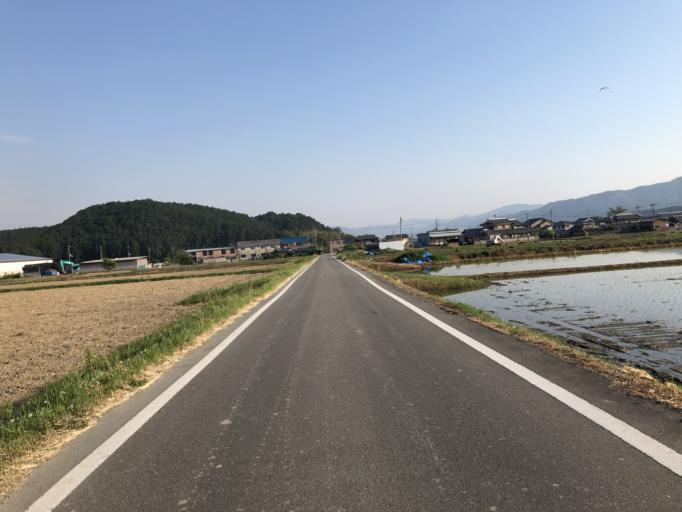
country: JP
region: Kyoto
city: Kameoka
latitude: 35.0742
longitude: 135.5568
